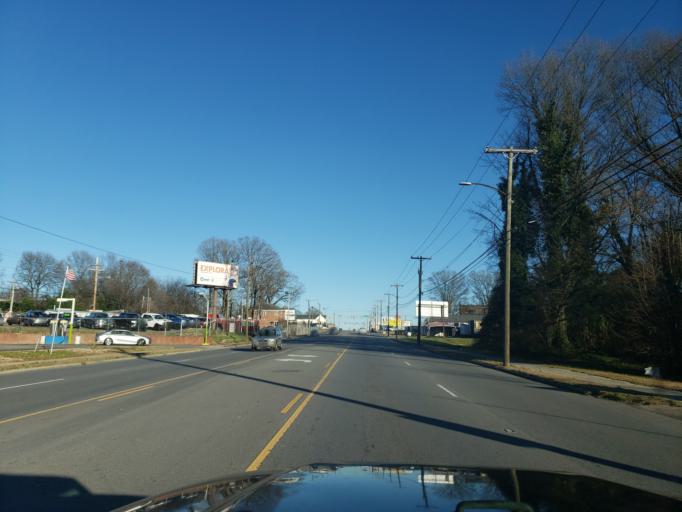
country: US
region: North Carolina
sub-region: Gaston County
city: Gastonia
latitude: 35.2603
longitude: -81.2110
